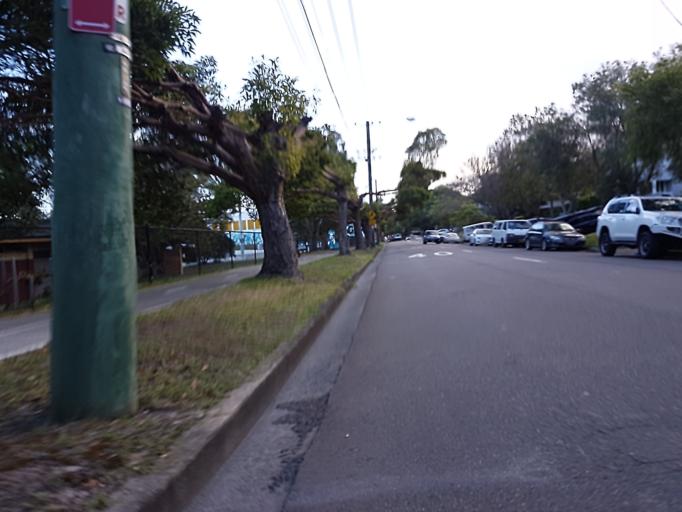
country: AU
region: New South Wales
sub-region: Manly Vale
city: Fairlight
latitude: -33.7905
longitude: 151.2775
